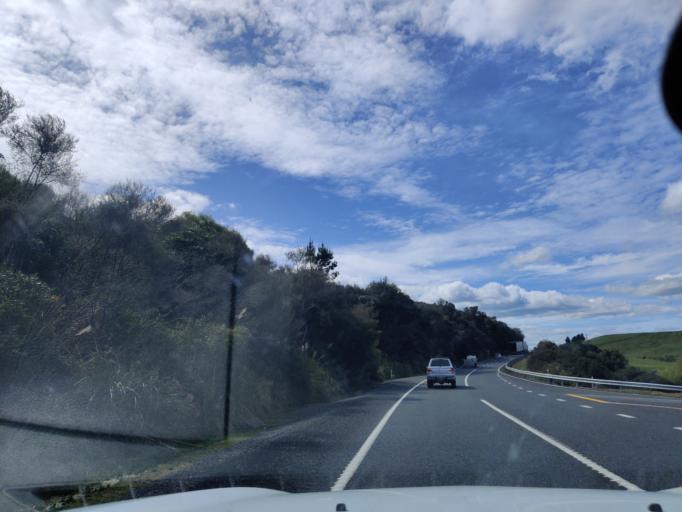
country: NZ
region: Waikato
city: Turangi
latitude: -39.0827
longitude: 175.3801
